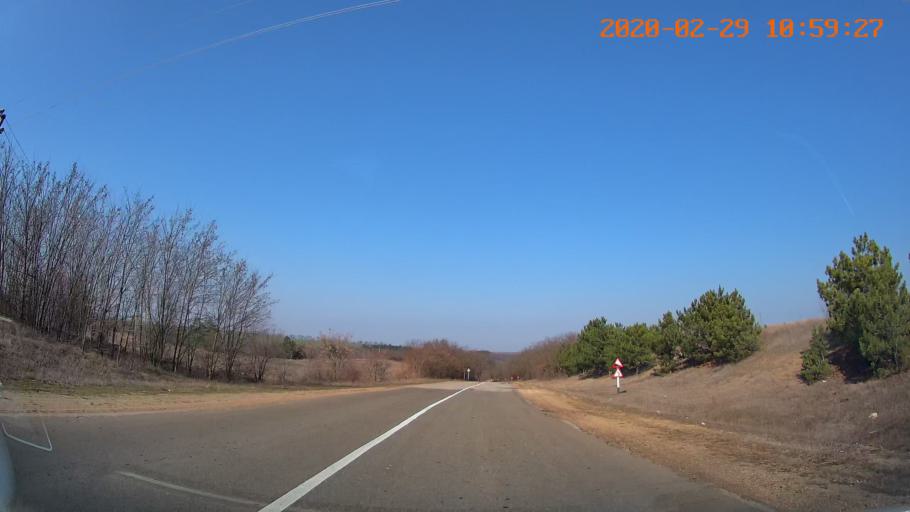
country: MD
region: Telenesti
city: Grigoriopol
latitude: 47.1655
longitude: 29.2914
